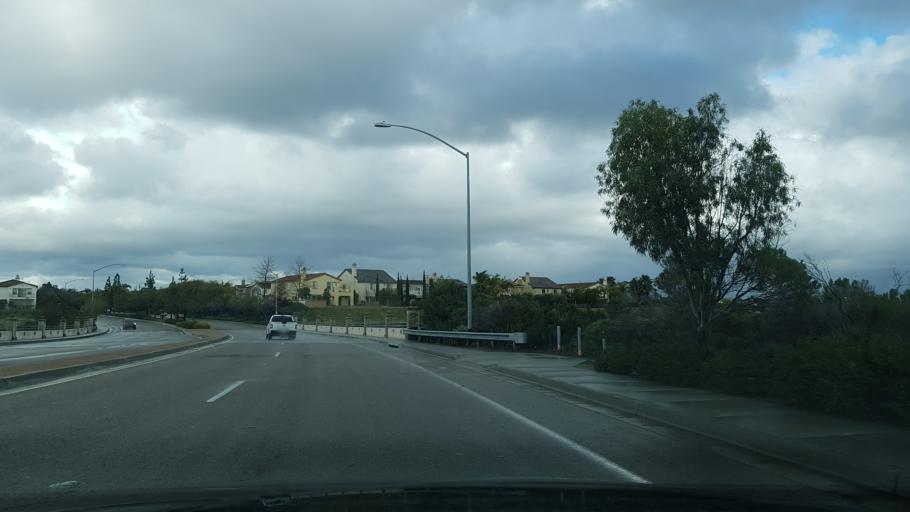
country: US
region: California
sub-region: San Diego County
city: Del Mar
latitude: 32.9224
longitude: -117.2110
